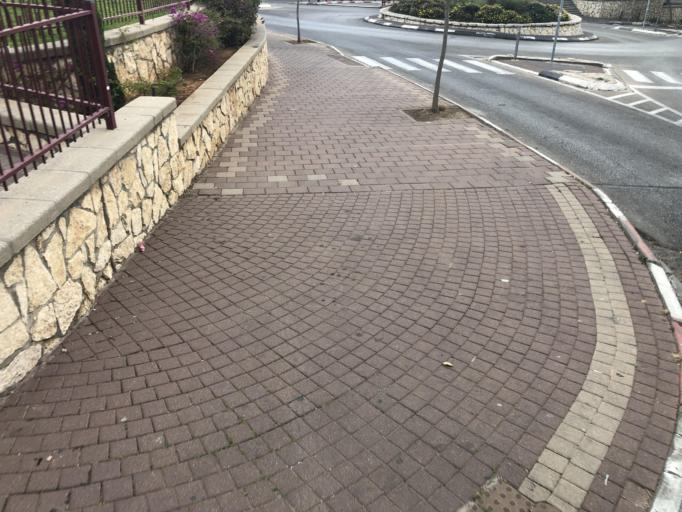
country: IL
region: Jerusalem
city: Modiin Ilit
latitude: 31.9398
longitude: 35.0383
